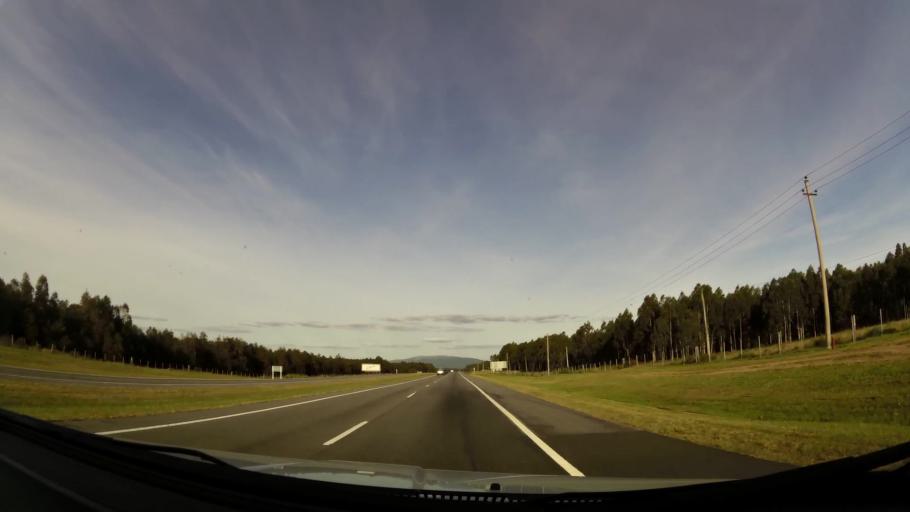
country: UY
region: Lavalleja
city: Solis de Mataojo
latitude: -34.7826
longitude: -55.4867
